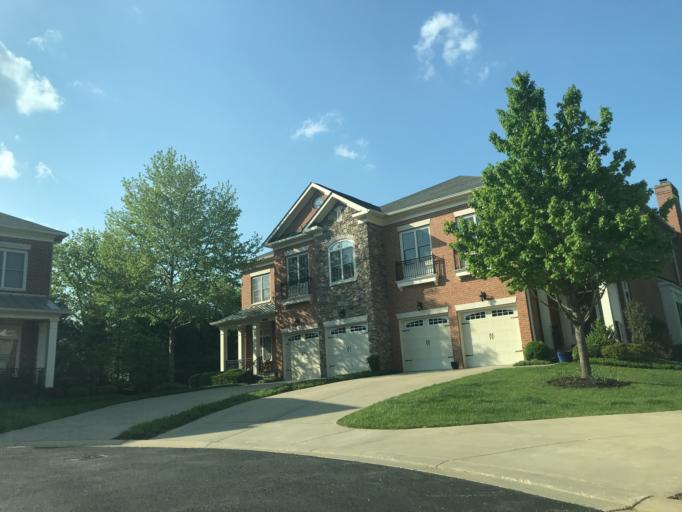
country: US
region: Maryland
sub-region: Baltimore County
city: Towson
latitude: 39.3840
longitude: -76.6242
